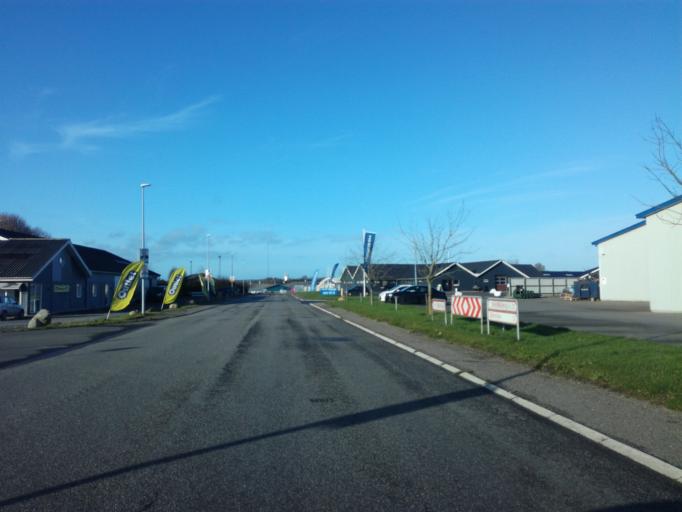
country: DK
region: South Denmark
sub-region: Vejle Kommune
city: Brejning
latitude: 55.6376
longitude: 9.6727
